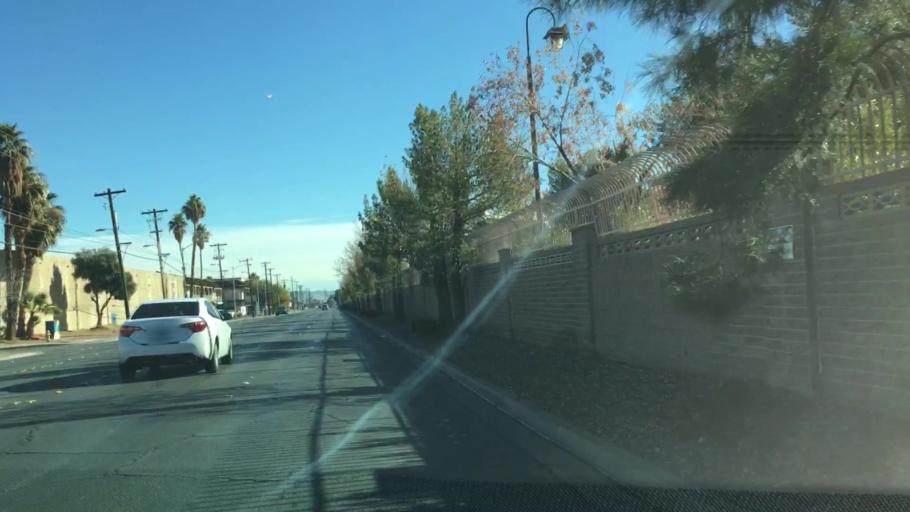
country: US
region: Nevada
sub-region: Clark County
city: Winchester
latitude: 36.1405
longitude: -115.1451
